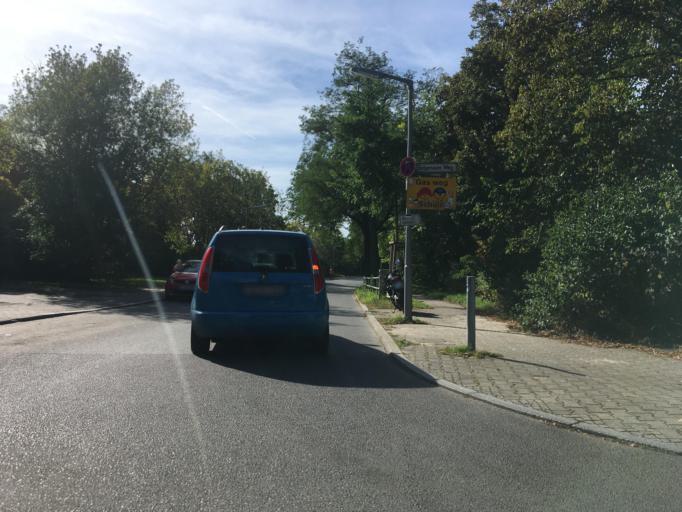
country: DE
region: Berlin
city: Altglienicke
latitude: 52.4145
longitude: 13.5103
